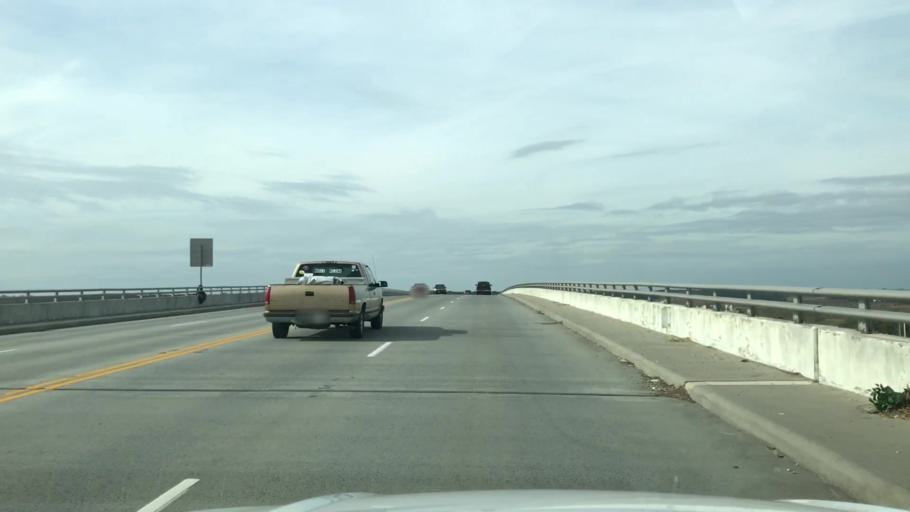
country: US
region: South Carolina
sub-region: Charleston County
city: Charleston
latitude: 32.7529
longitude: -80.0094
